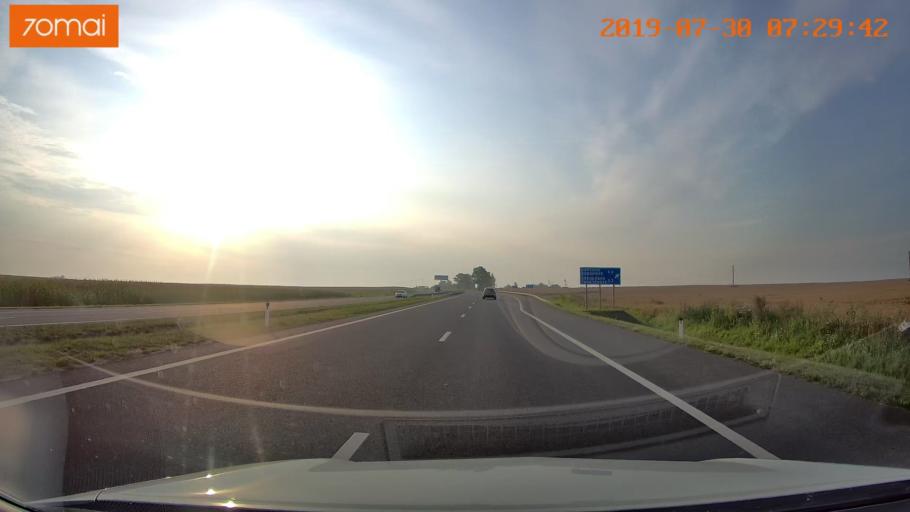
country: RU
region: Kaliningrad
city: Gvardeysk
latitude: 54.6711
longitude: 20.9467
